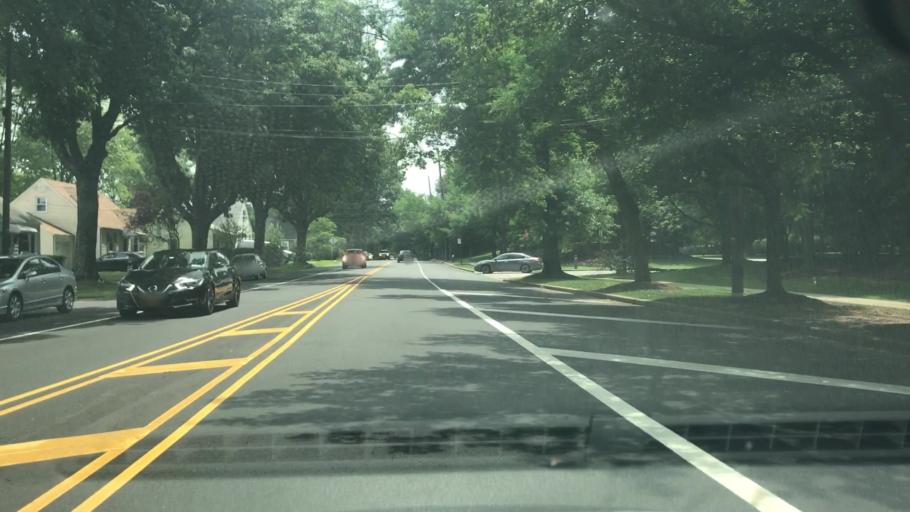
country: US
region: New Jersey
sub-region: Union County
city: Clark
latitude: 40.6387
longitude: -74.3052
